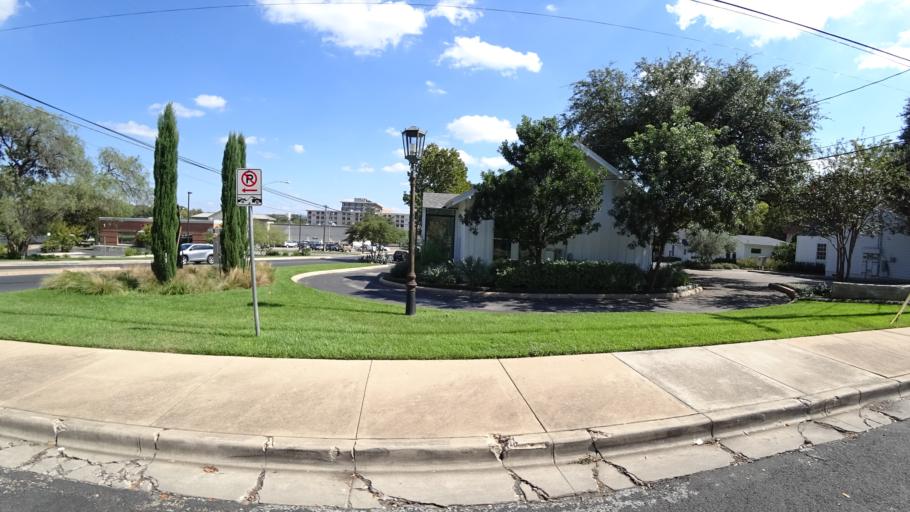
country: US
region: Texas
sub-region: Travis County
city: Austin
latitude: 30.3067
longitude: -97.7506
